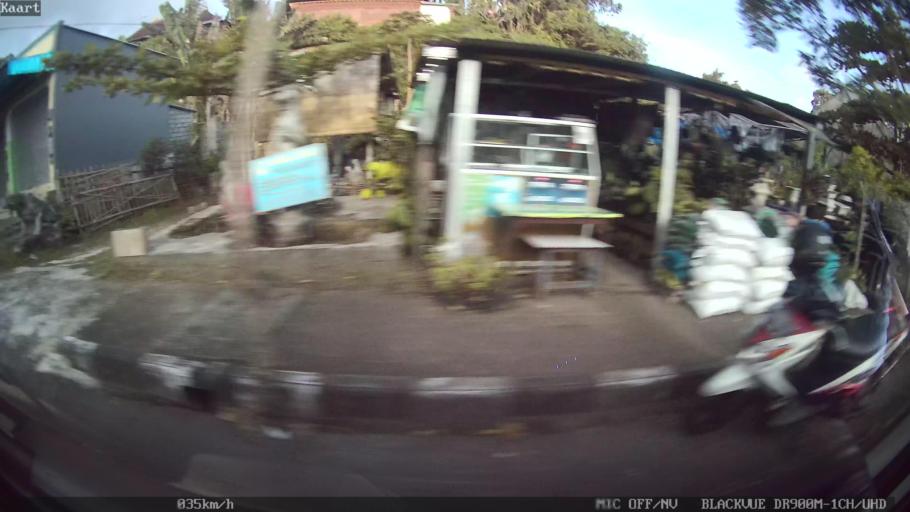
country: ID
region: Bali
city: Banjar Parekan
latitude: -8.5828
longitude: 115.2155
